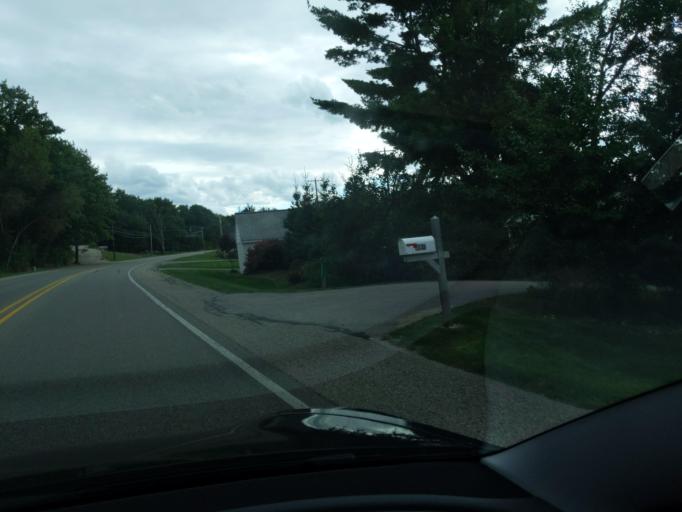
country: US
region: Michigan
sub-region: Kalkaska County
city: Rapid City
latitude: 44.8698
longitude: -85.2777
